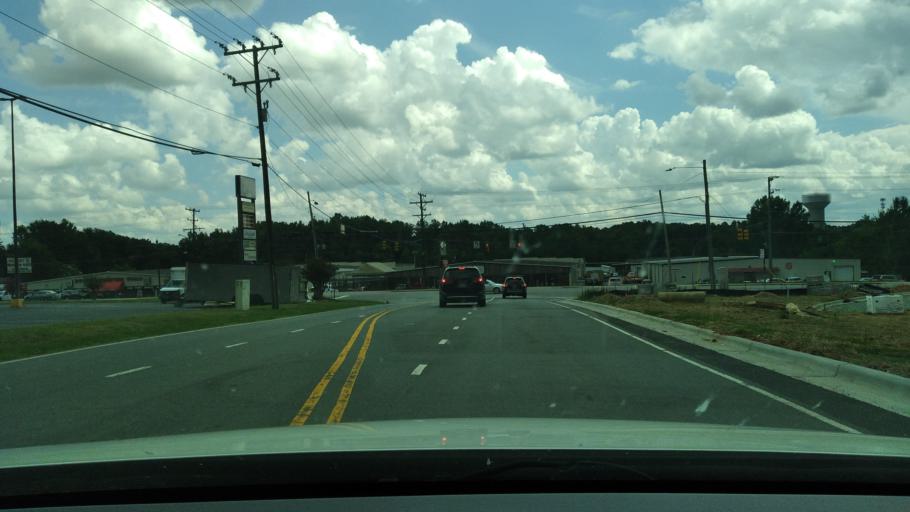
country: US
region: North Carolina
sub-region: Alamance County
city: Elon
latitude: 36.0810
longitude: -79.5168
